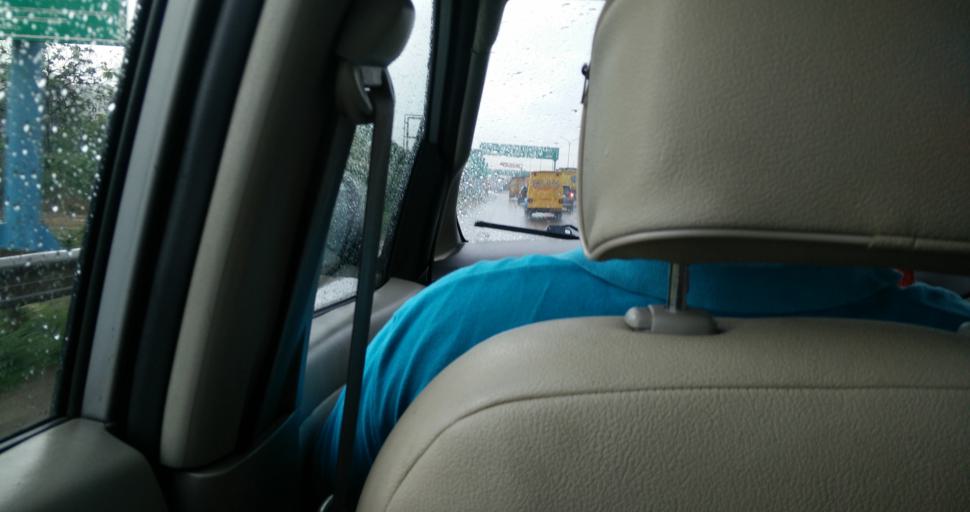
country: IN
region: Tamil Nadu
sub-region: Kancheepuram
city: Sriperumbudur
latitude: 12.9806
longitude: 79.9659
